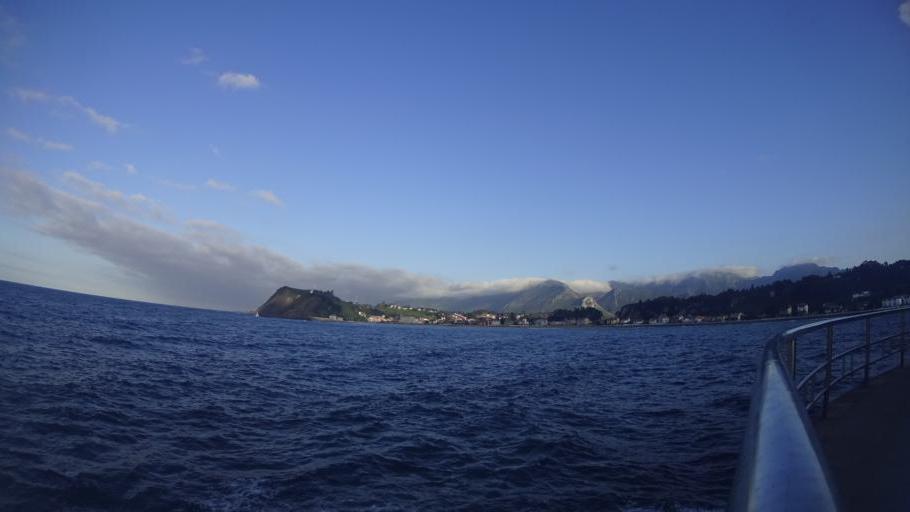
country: ES
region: Asturias
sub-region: Province of Asturias
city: Ribadesella
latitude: 43.4704
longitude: -5.0752
